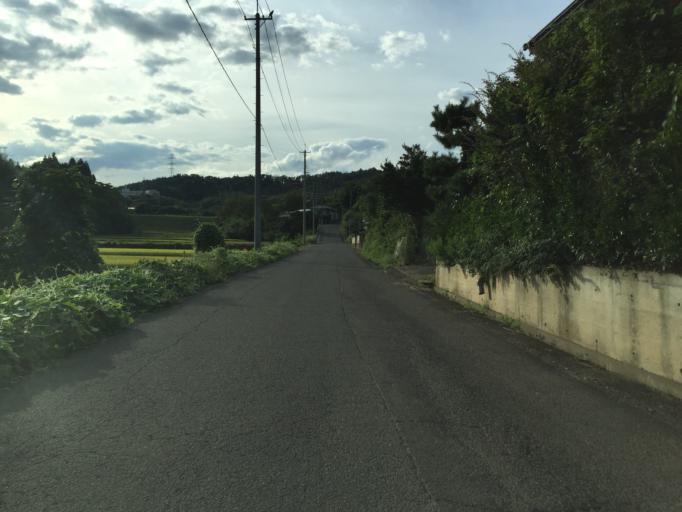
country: JP
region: Fukushima
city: Hobaramachi
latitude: 37.7966
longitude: 140.5321
